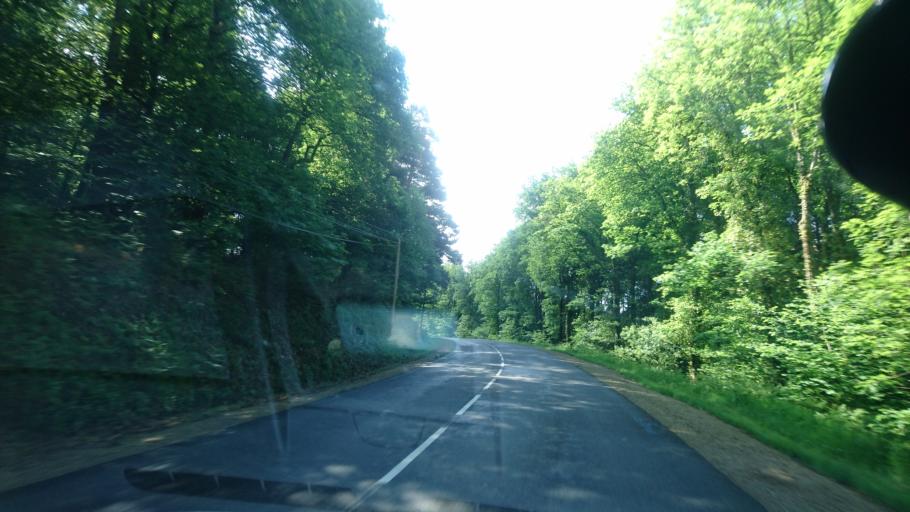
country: FR
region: Limousin
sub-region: Departement de la Haute-Vienne
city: Peyrat-le-Chateau
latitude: 45.8073
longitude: 1.8241
